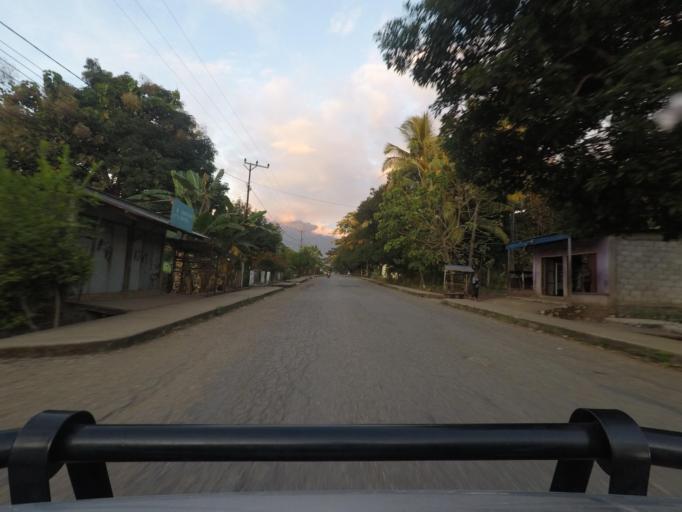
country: TL
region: Bobonaro
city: Maliana
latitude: -8.9912
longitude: 125.1976
